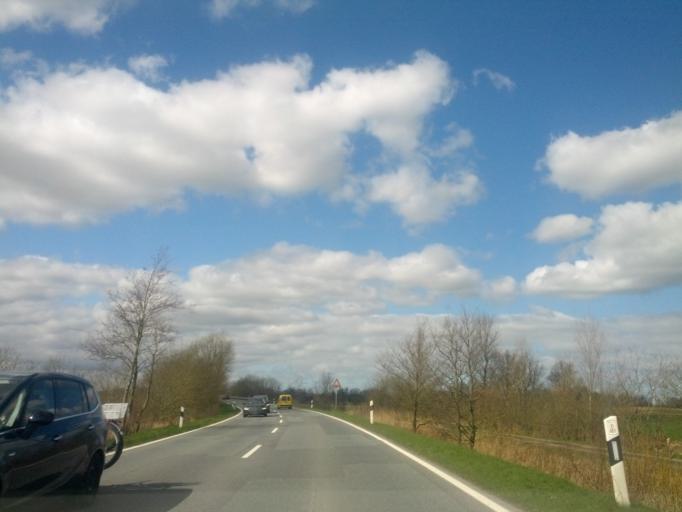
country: DE
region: Lower Saxony
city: Wittmund
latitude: 53.5847
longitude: 7.7949
